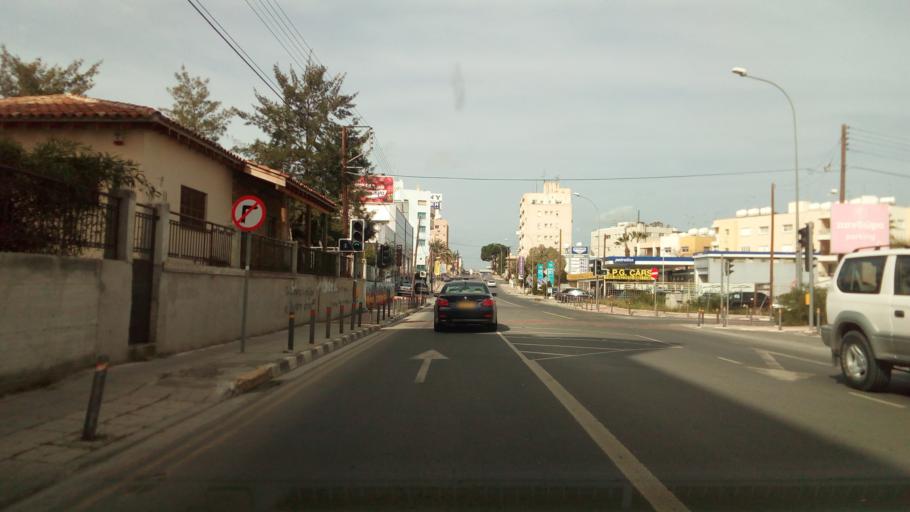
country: CY
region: Lefkosia
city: Nicosia
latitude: 35.1481
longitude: 33.3528
